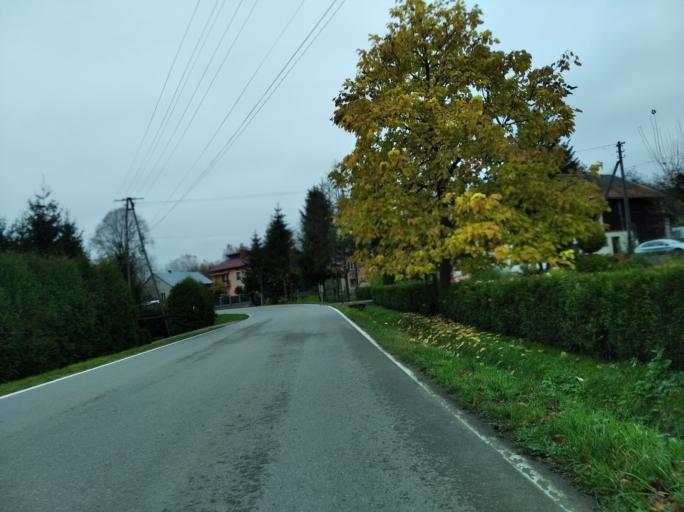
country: PL
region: Subcarpathian Voivodeship
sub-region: Powiat krosnienski
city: Leki
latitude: 49.8099
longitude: 21.6580
